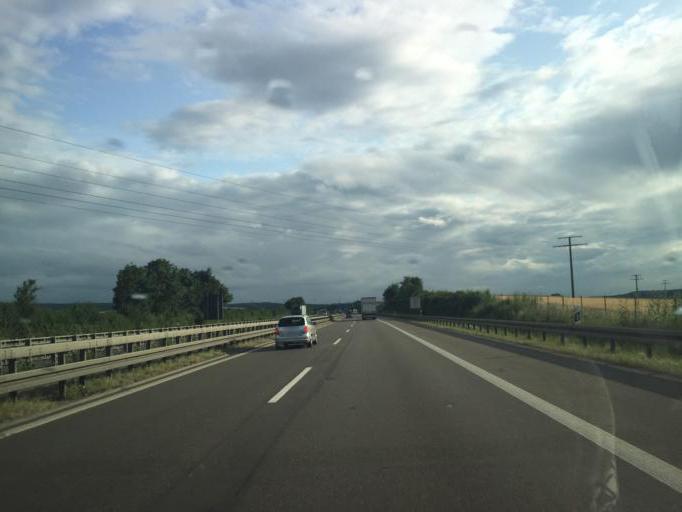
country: DE
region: Baden-Wuerttemberg
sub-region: Regierungsbezirk Stuttgart
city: Gartringen
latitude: 48.6233
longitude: 8.9122
